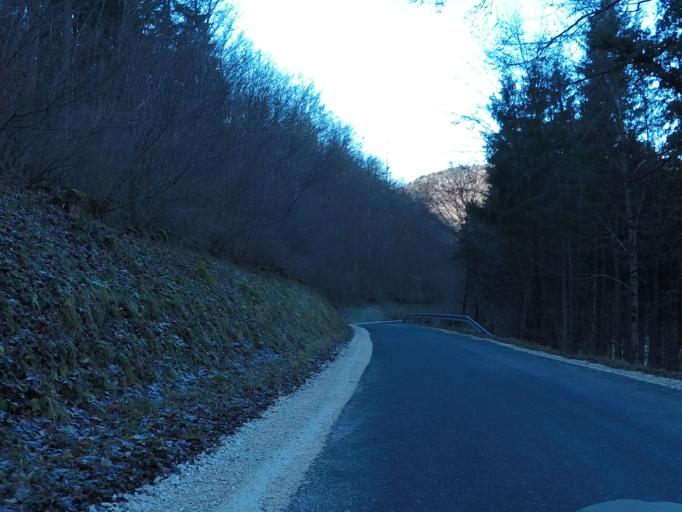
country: DE
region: Baden-Wuerttemberg
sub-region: Tuebingen Region
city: Eningen unter Achalm
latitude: 48.4465
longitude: 9.2896
